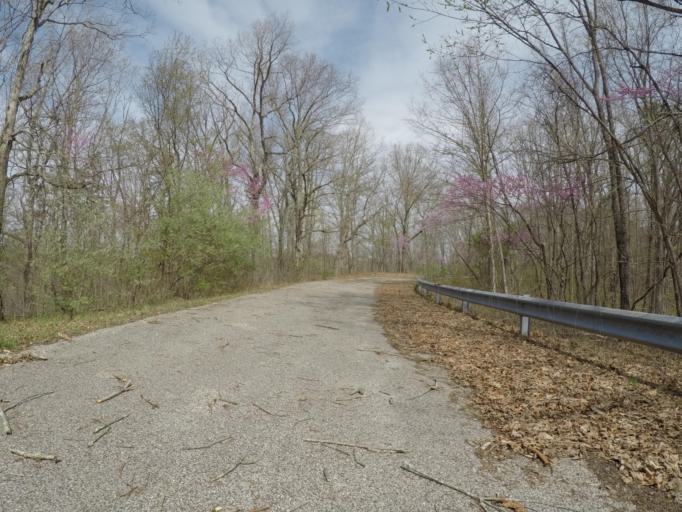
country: US
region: West Virginia
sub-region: Wayne County
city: Lavalette
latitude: 38.3185
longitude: -82.3514
